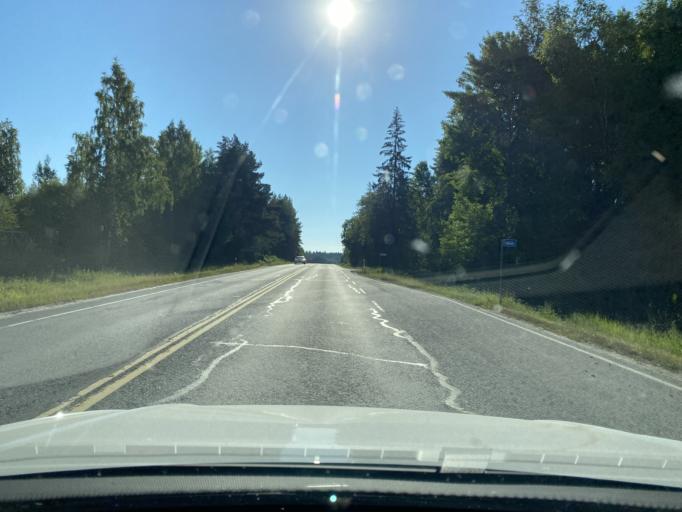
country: FI
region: Haeme
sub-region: Forssa
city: Tammela
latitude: 60.8302
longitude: 23.6974
